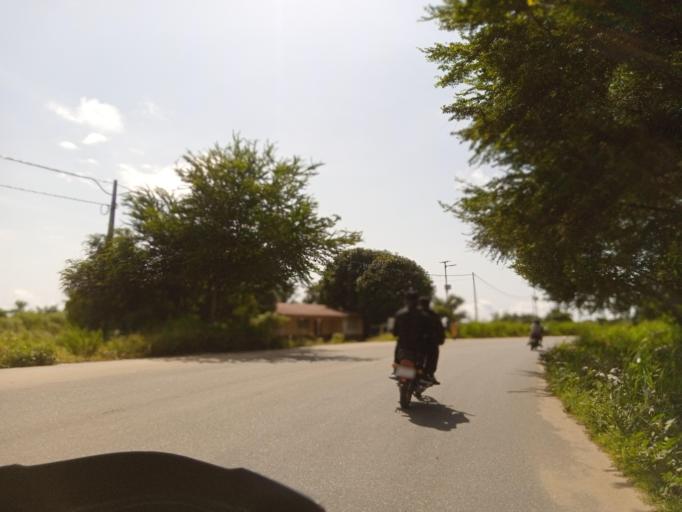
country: SL
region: Northern Province
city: Tintafor
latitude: 8.6182
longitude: -13.2101
